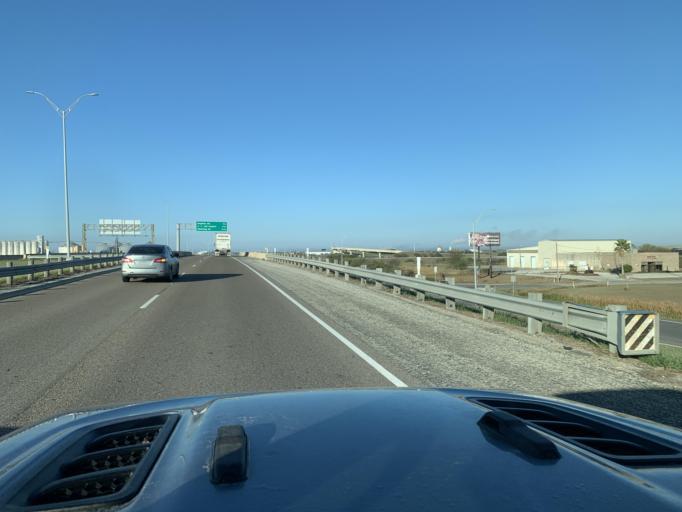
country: US
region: Texas
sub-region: Nueces County
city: Corpus Christi
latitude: 27.7819
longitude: -97.4767
